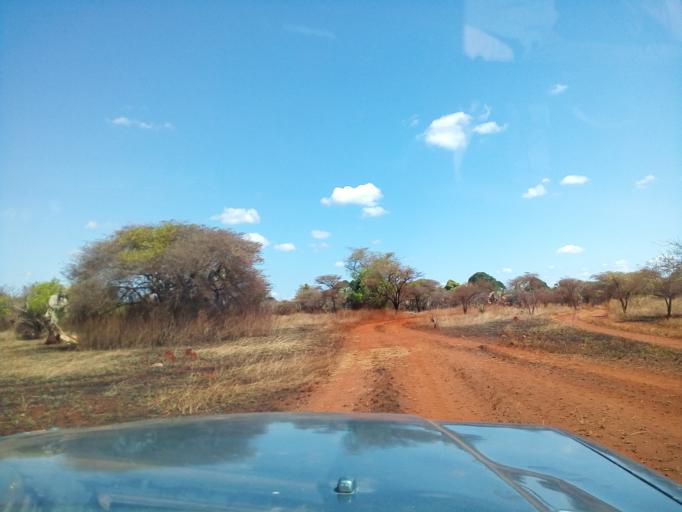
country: MG
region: Boeny
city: Mahajanga
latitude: -15.9910
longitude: 46.0235
